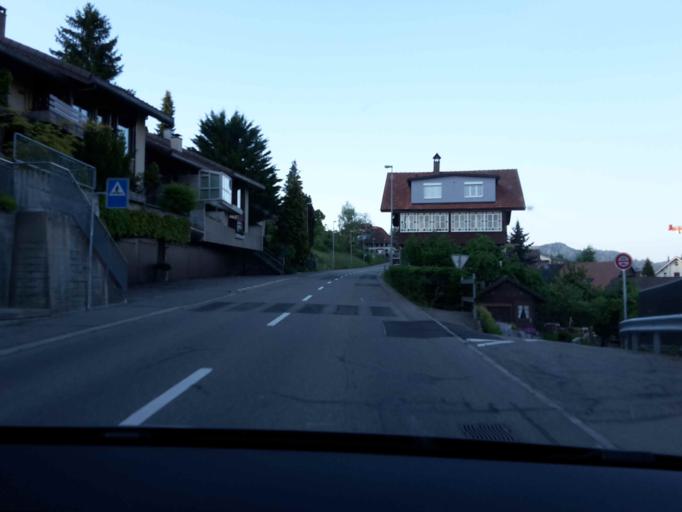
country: CH
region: Bern
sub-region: Bern-Mittelland District
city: Konolfingen
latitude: 46.8890
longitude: 7.6302
